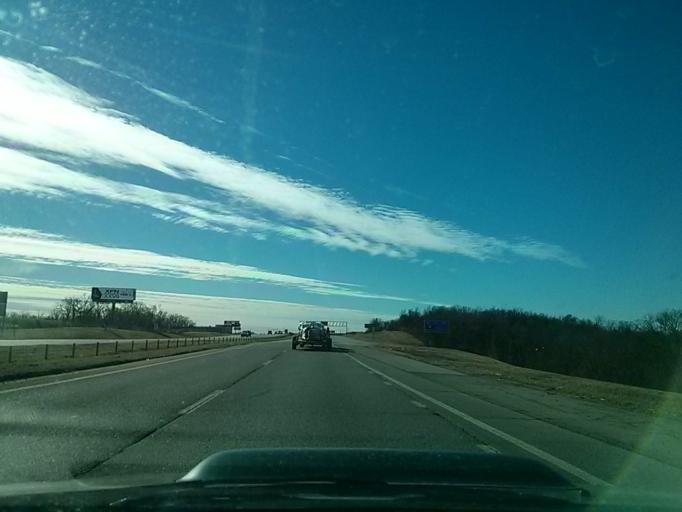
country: US
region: Oklahoma
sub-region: Tulsa County
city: Oakhurst
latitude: 36.0703
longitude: -96.0068
